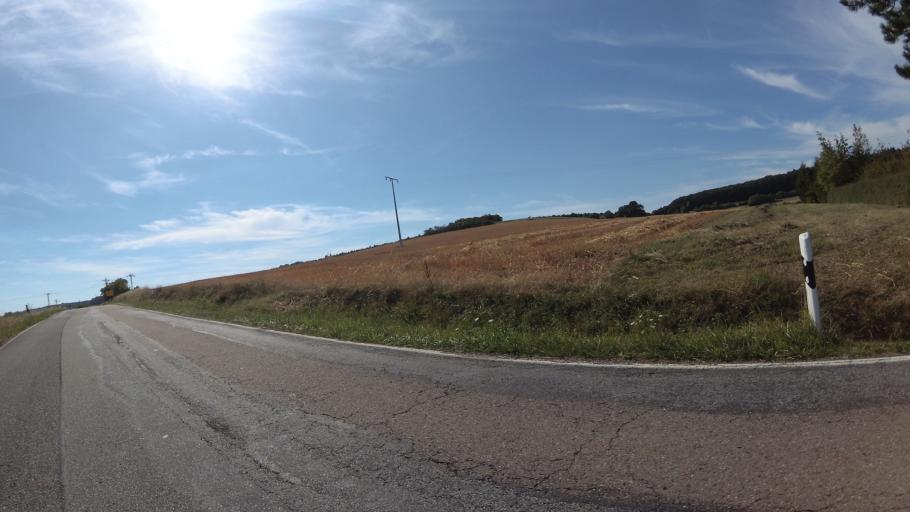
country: DE
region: Saarland
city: Blieskastel
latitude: 49.1646
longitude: 7.2822
